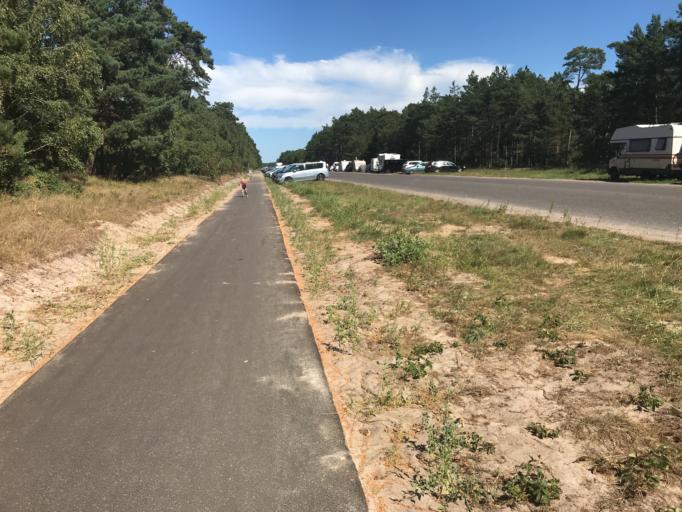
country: PL
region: West Pomeranian Voivodeship
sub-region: Powiat slawienski
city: Darlowo
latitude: 54.5229
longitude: 16.5001
